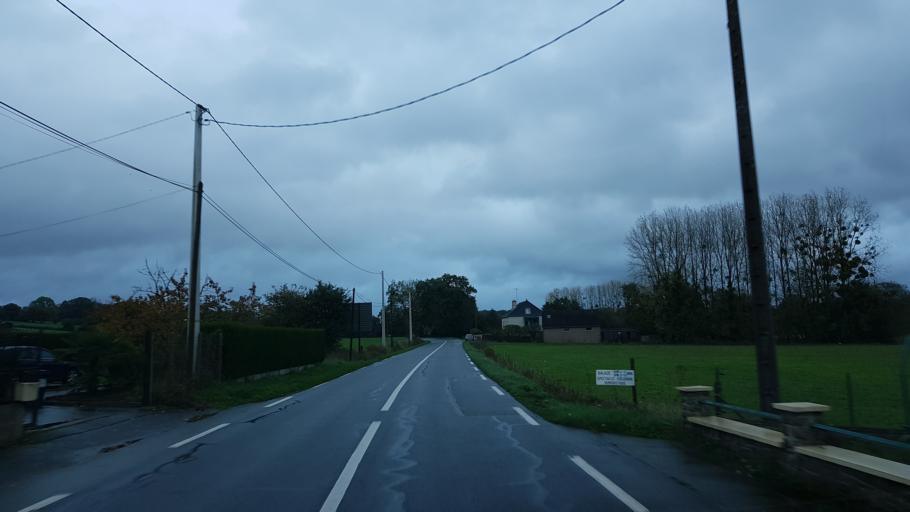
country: FR
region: Brittany
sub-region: Departement d'Ille-et-Vilaine
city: Vitre
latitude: 48.1316
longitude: -1.1913
